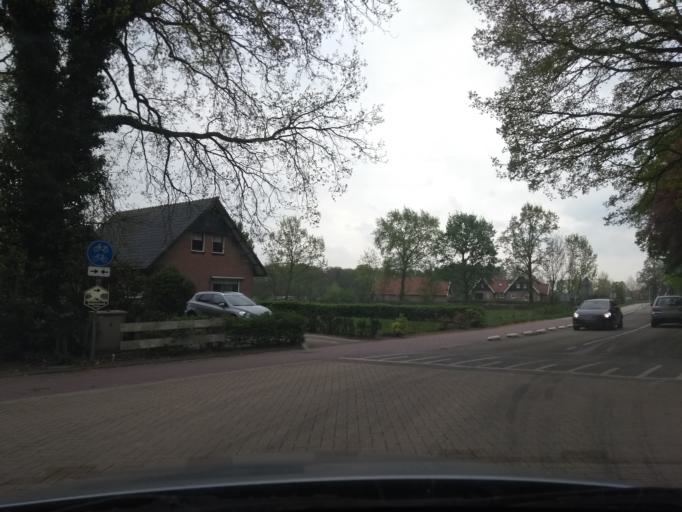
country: DE
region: Lower Saxony
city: Lage
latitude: 52.4208
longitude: 6.9102
